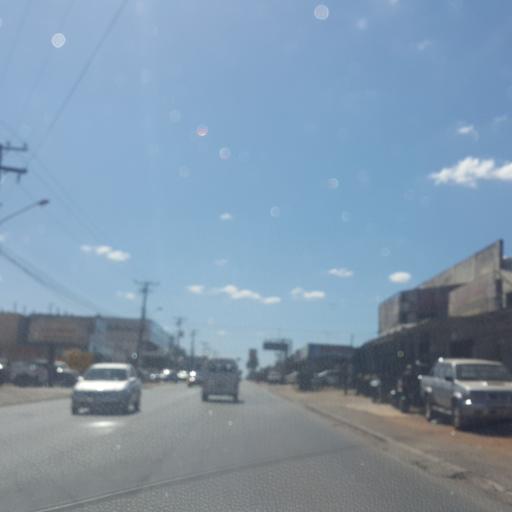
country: BR
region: Federal District
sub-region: Brasilia
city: Brasilia
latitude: -15.8113
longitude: -48.0727
